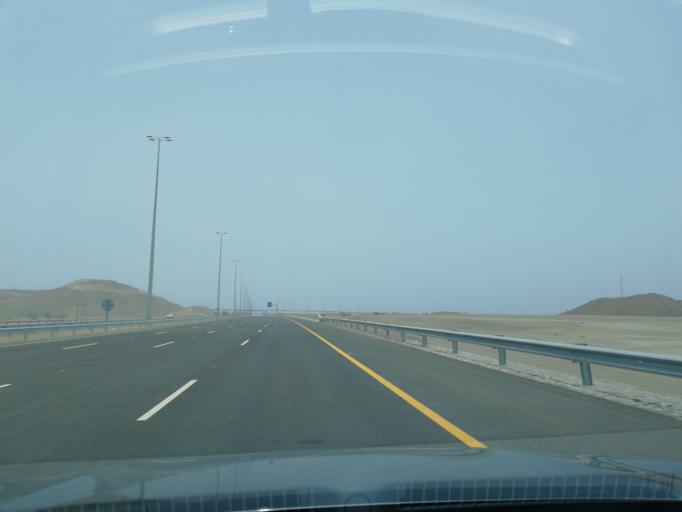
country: OM
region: Al Batinah
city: Al Liwa'
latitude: 24.5197
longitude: 56.5045
